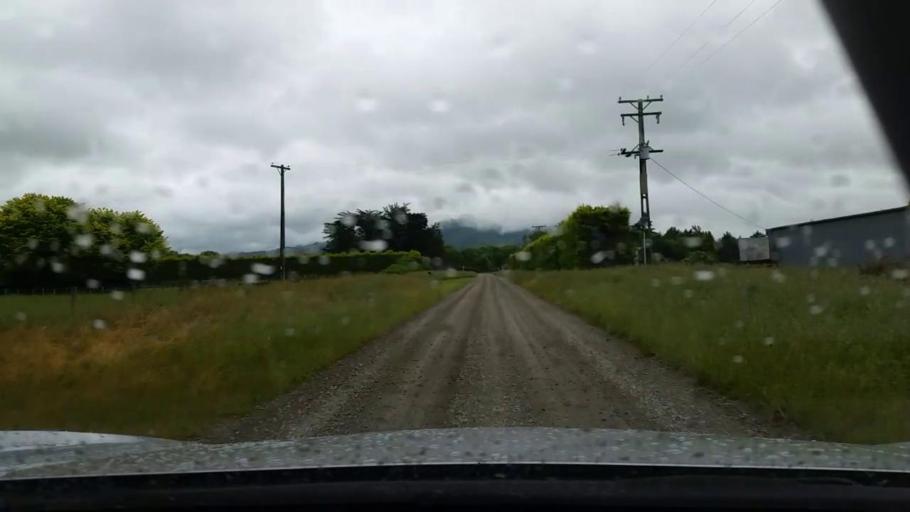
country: NZ
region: Southland
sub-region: Gore District
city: Gore
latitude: -46.0708
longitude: 168.9552
